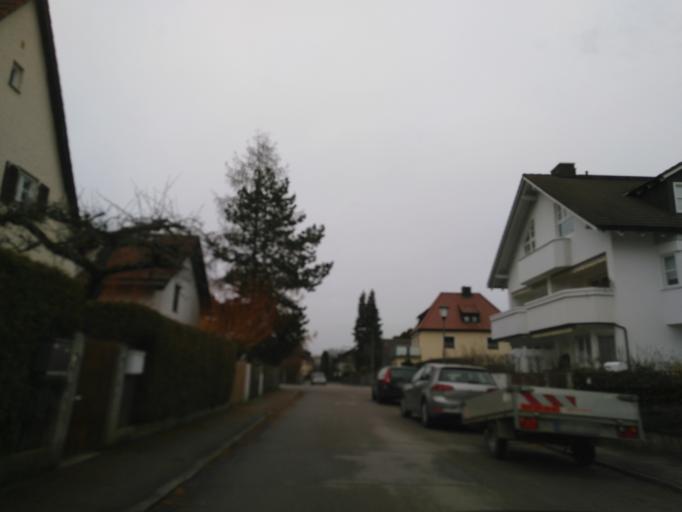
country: DE
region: Bavaria
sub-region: Upper Bavaria
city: Neubiberg
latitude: 48.1315
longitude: 11.6738
